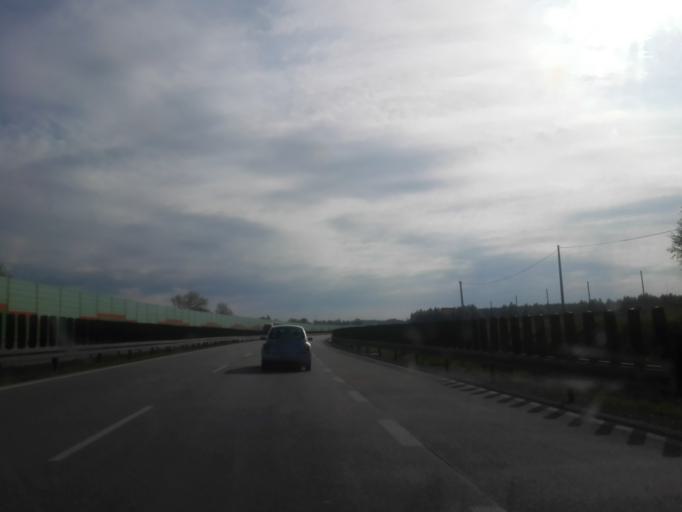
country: PL
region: Lodz Voivodeship
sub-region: Powiat tomaszowski
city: Ujazd
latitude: 51.5211
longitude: 19.9218
